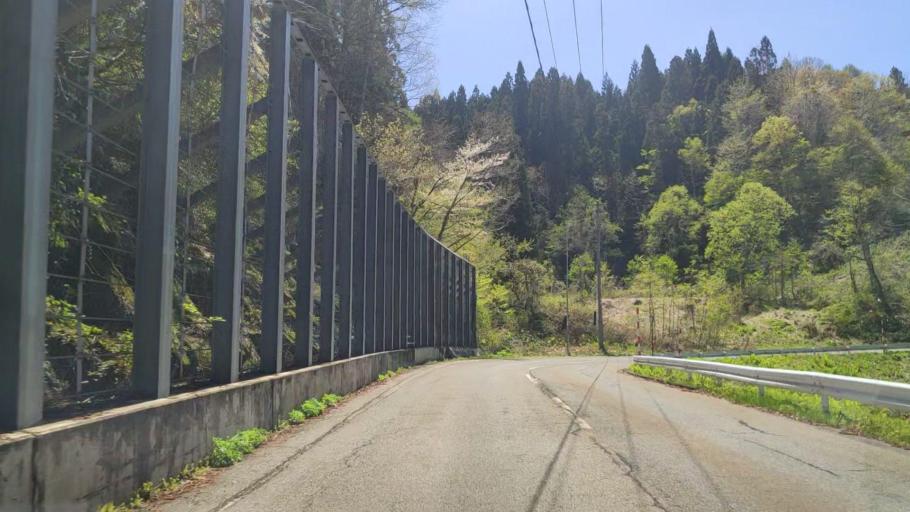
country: JP
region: Yamagata
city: Shinjo
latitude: 38.9730
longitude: 140.3553
